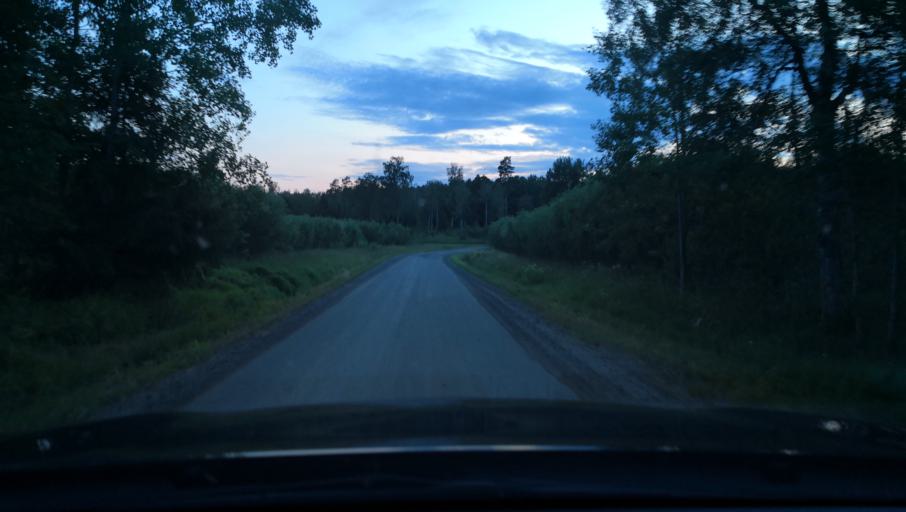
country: SE
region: Uppsala
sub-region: Osthammars Kommun
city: Bjorklinge
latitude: 60.0036
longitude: 17.3429
